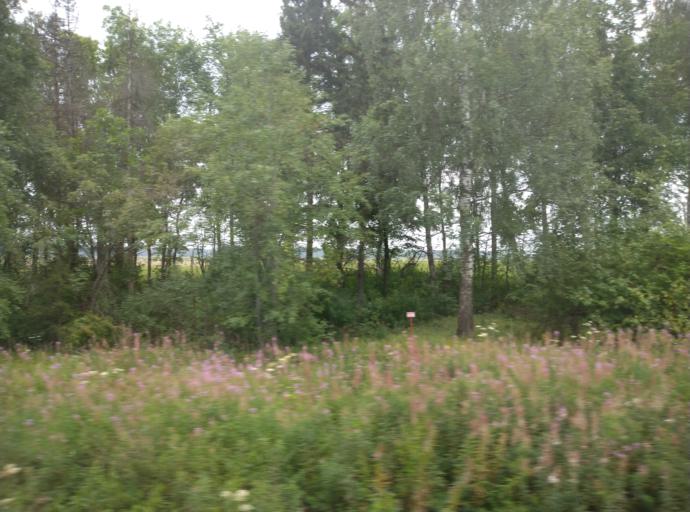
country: RU
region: Kostroma
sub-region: Kostromskoy Rayon
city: Kostroma
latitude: 57.7173
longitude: 40.8781
